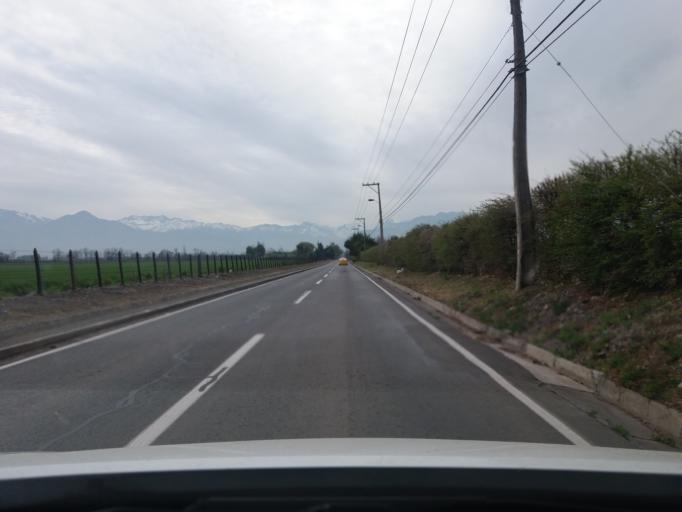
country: CL
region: Valparaiso
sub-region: Provincia de San Felipe
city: San Felipe
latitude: -32.8192
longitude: -70.6814
